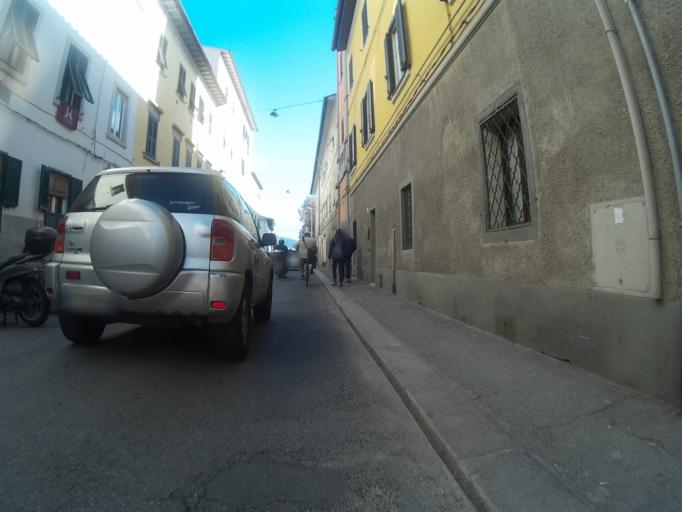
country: IT
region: Tuscany
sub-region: Provincia di Livorno
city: Livorno
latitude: 43.5500
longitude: 10.3198
